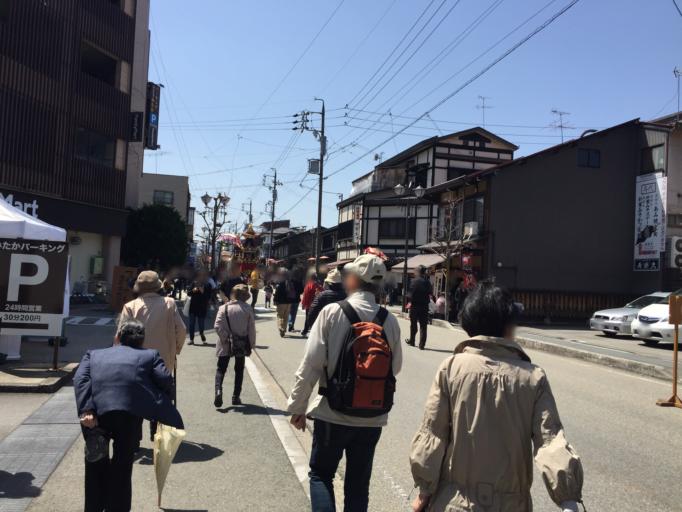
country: JP
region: Gifu
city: Takayama
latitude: 36.1416
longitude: 137.2608
